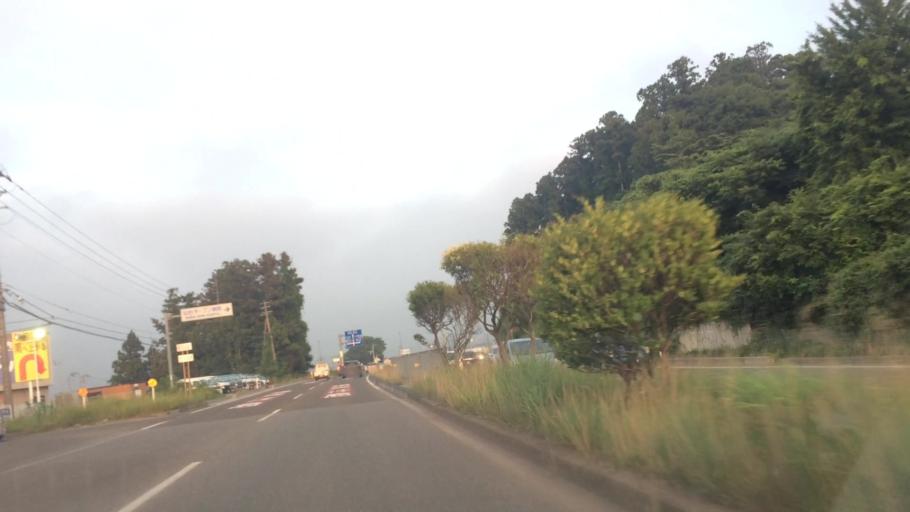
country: JP
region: Miyagi
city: Sendai-shi
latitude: 38.3038
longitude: 140.9177
